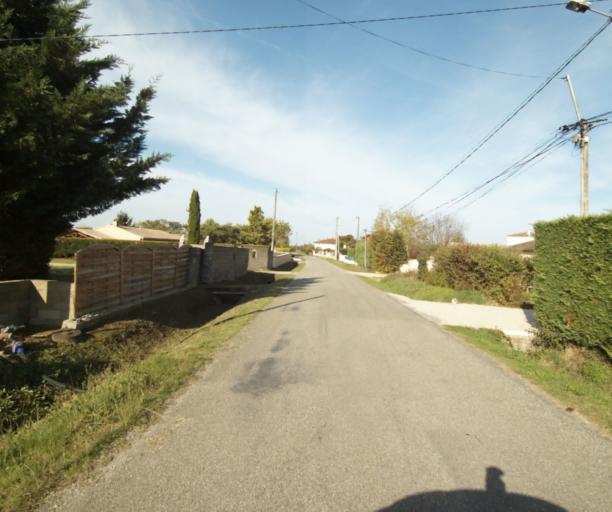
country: FR
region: Midi-Pyrenees
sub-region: Departement du Tarn-et-Garonne
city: Nohic
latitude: 43.9115
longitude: 1.4432
